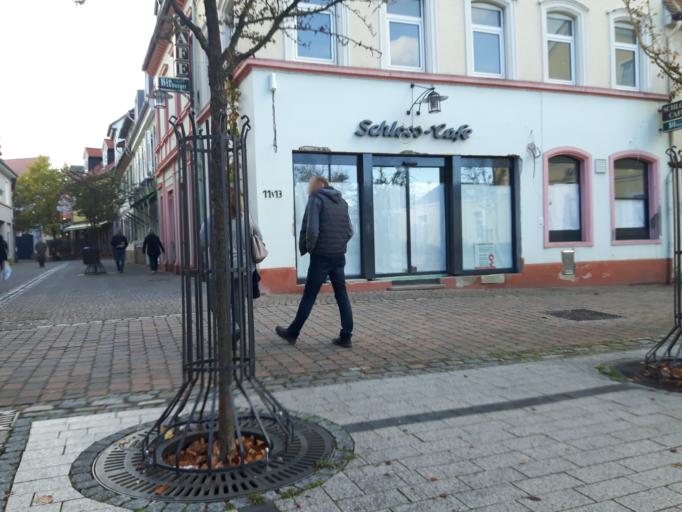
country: DE
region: Rheinland-Pfalz
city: Bad Duerkheim
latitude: 49.4622
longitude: 8.1686
